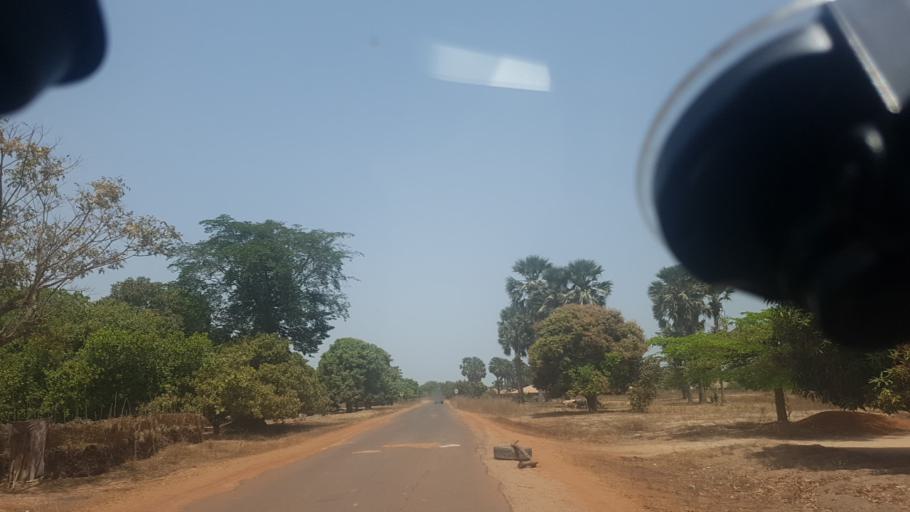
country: GW
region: Cacheu
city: Canchungo
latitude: 12.2797
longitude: -15.7854
